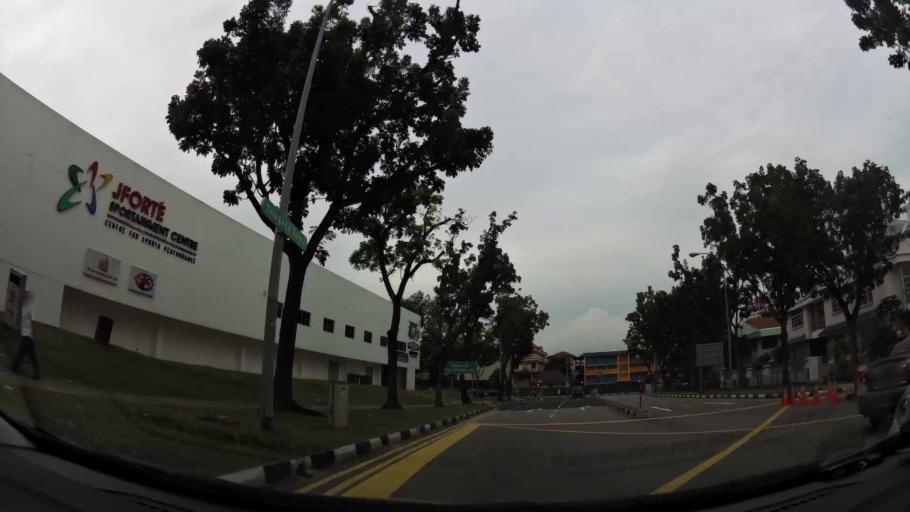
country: SG
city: Singapore
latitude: 1.3601
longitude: 103.8885
